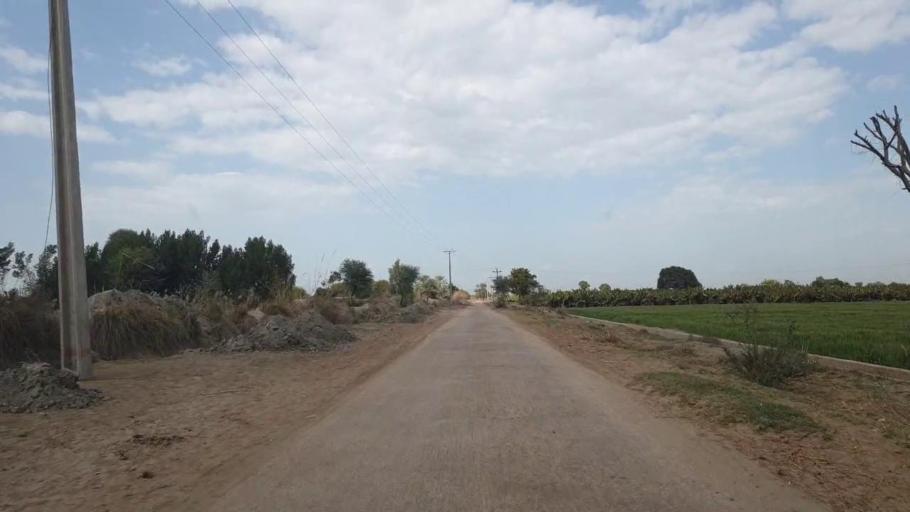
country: PK
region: Sindh
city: Shahdadpur
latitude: 25.9661
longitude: 68.4767
